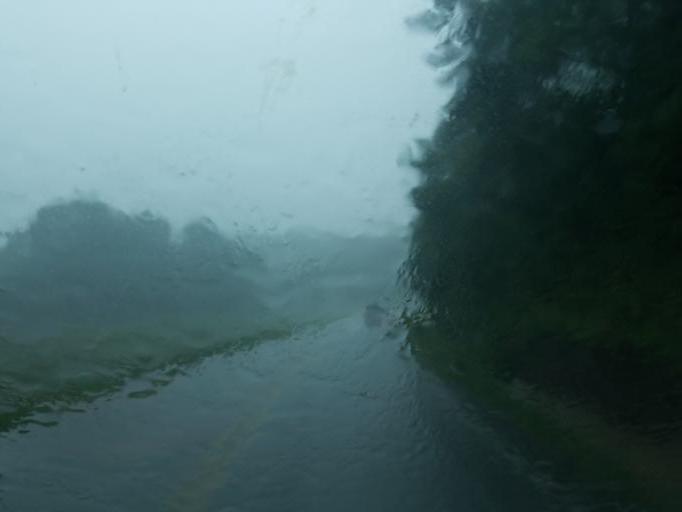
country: US
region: Kentucky
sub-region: Carter County
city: Olive Hill
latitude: 38.3548
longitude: -83.1978
